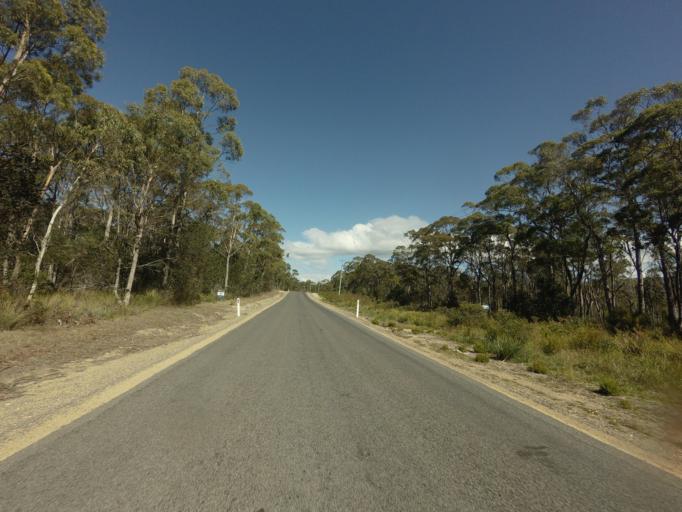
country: AU
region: Tasmania
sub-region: Break O'Day
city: St Helens
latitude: -41.6038
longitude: 148.2057
